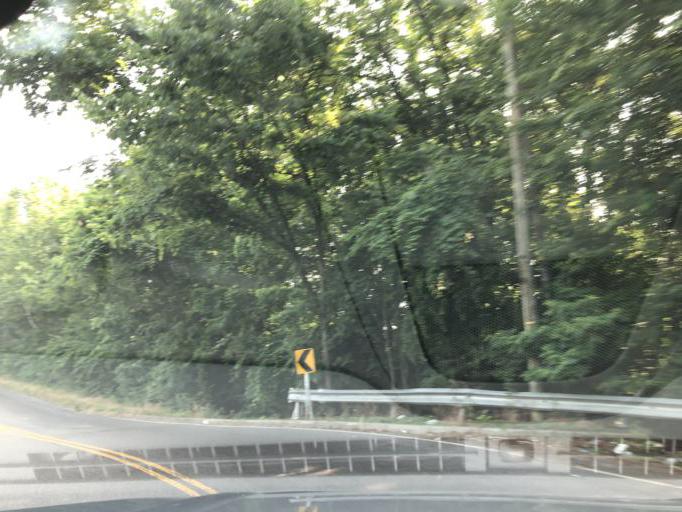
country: US
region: Tennessee
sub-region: Rutherford County
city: La Vergne
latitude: 36.0550
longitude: -86.6366
